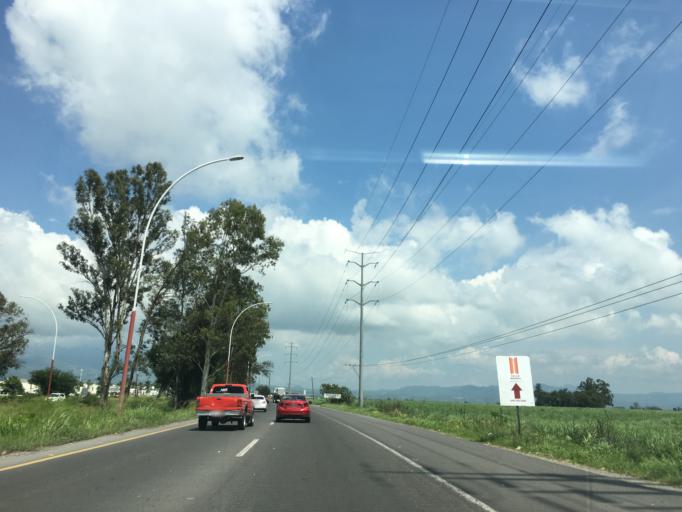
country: MX
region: Nayarit
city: Xalisco
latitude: 21.4678
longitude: -104.8843
